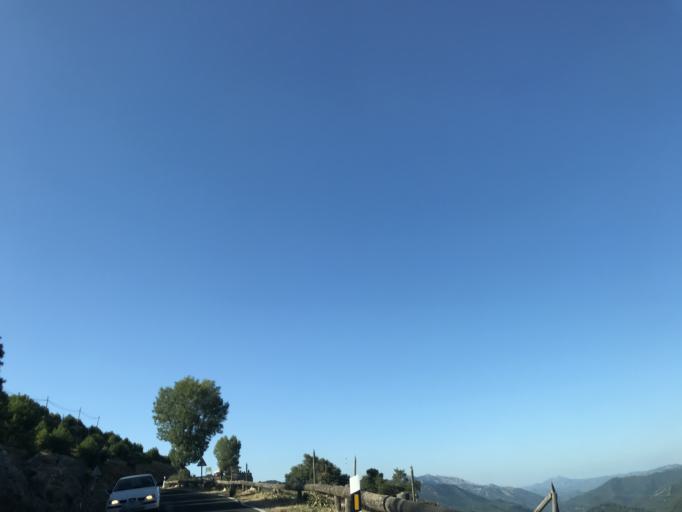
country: ES
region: Andalusia
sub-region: Provincia de Jaen
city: La Iruela
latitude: 37.9390
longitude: -2.9393
